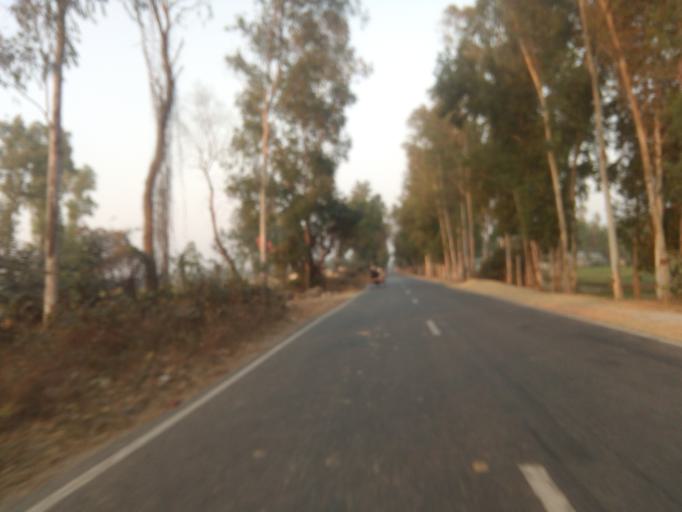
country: BD
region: Rajshahi
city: Bogra
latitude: 24.6336
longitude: 89.2475
